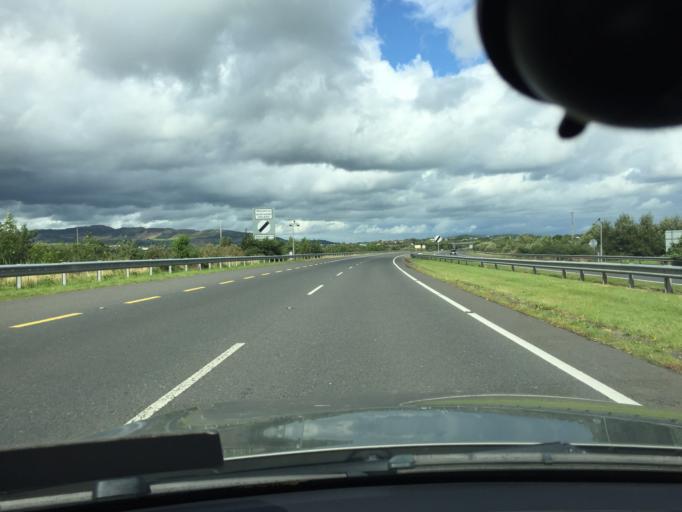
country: GB
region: Northern Ireland
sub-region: Newry and Mourne District
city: Newry
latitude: 54.1130
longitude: -6.3653
